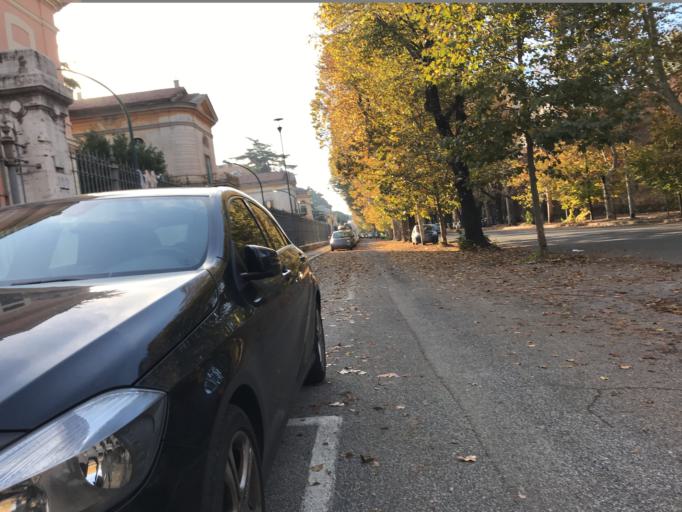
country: IT
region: Latium
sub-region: Citta metropolitana di Roma Capitale
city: Rome
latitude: 41.9086
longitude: 12.5087
